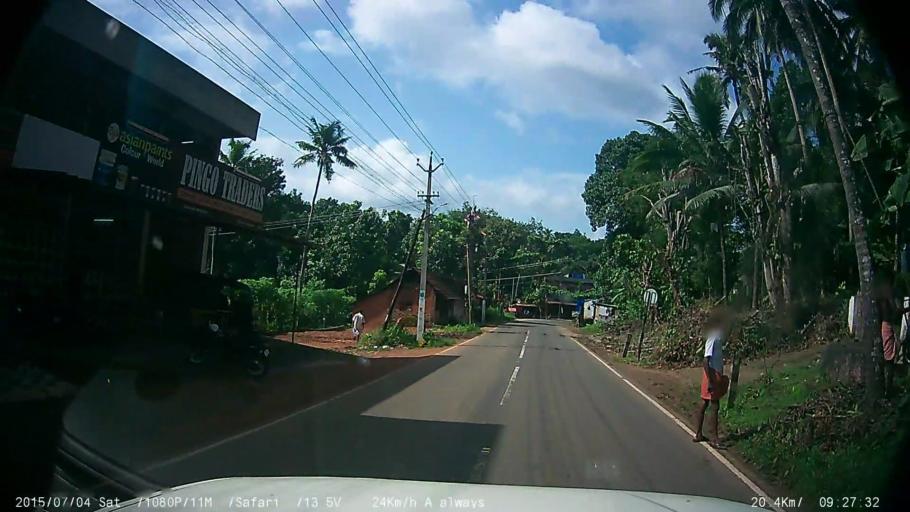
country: IN
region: Kerala
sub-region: Kottayam
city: Palackattumala
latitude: 9.6501
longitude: 76.6124
